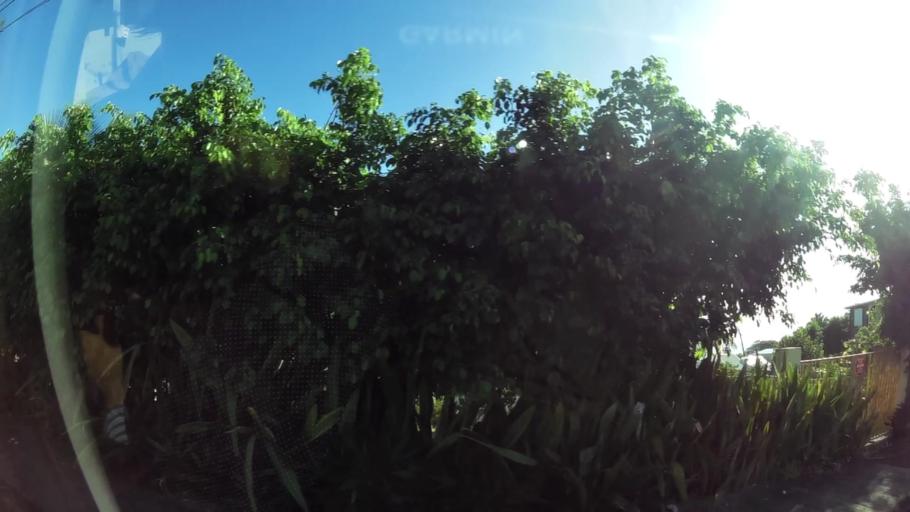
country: GP
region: Guadeloupe
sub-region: Guadeloupe
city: Le Gosier
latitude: 16.2031
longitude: -61.4765
